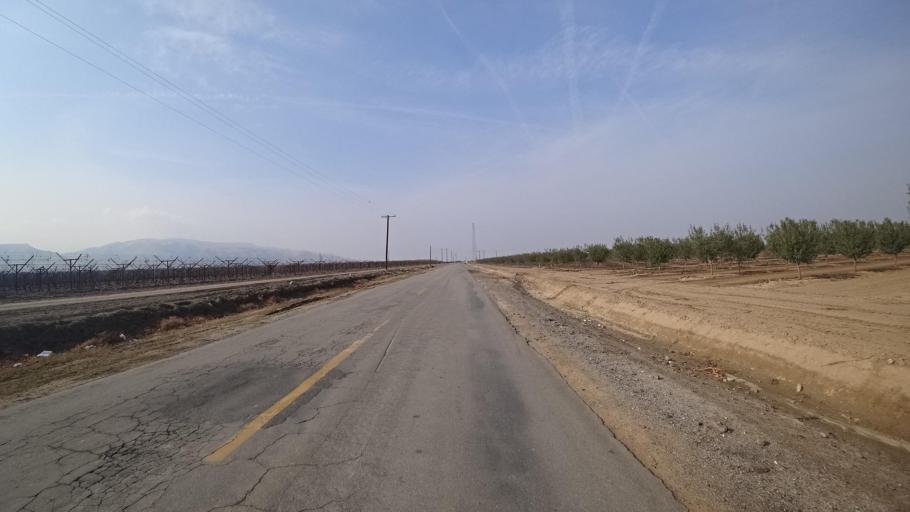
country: US
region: California
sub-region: Kern County
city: Weedpatch
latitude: 35.0336
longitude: -118.9543
